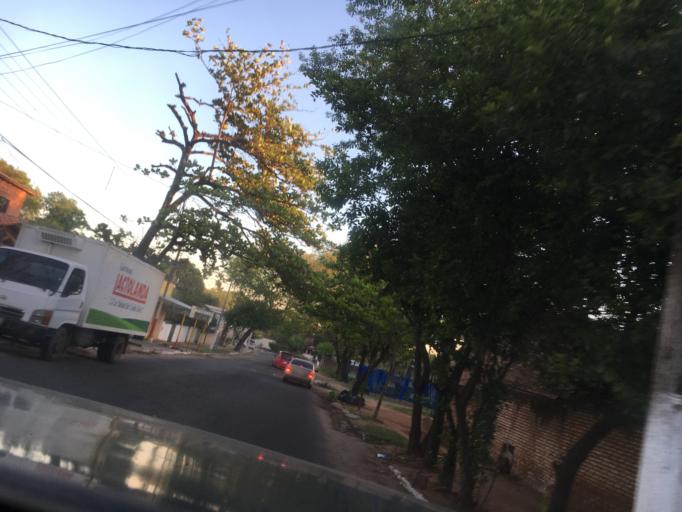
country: PY
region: Central
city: Lambare
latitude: -25.3235
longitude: -57.6111
